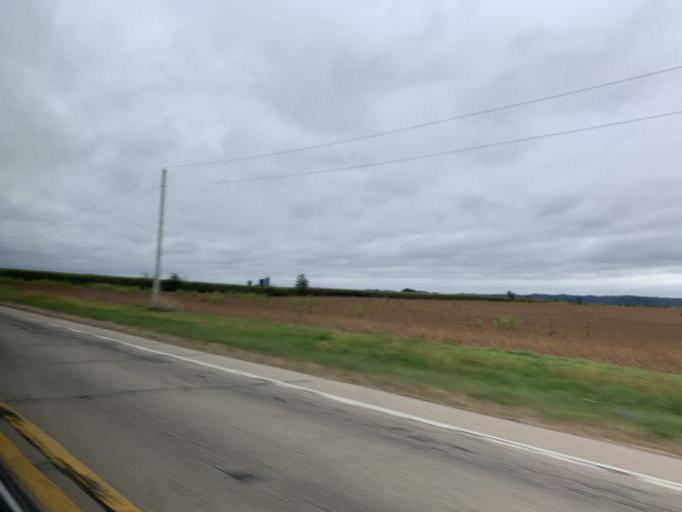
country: US
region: Wisconsin
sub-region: Grant County
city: Muscoda
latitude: 43.2197
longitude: -90.4705
